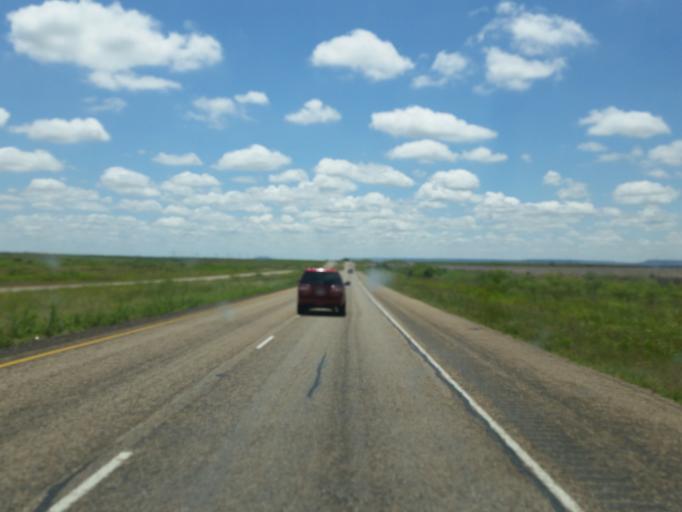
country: US
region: Texas
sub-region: Garza County
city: Post
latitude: 33.1165
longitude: -101.2770
